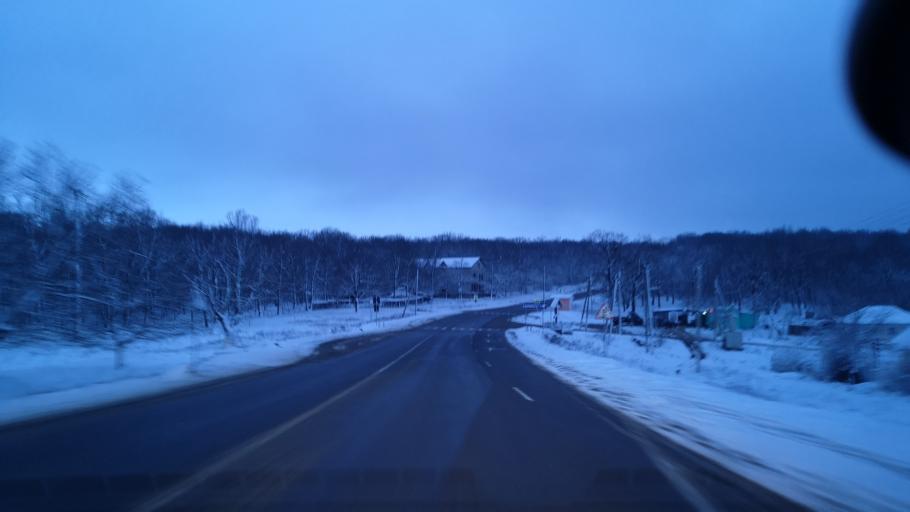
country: MD
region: Rezina
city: Rezina
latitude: 47.7333
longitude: 28.8762
